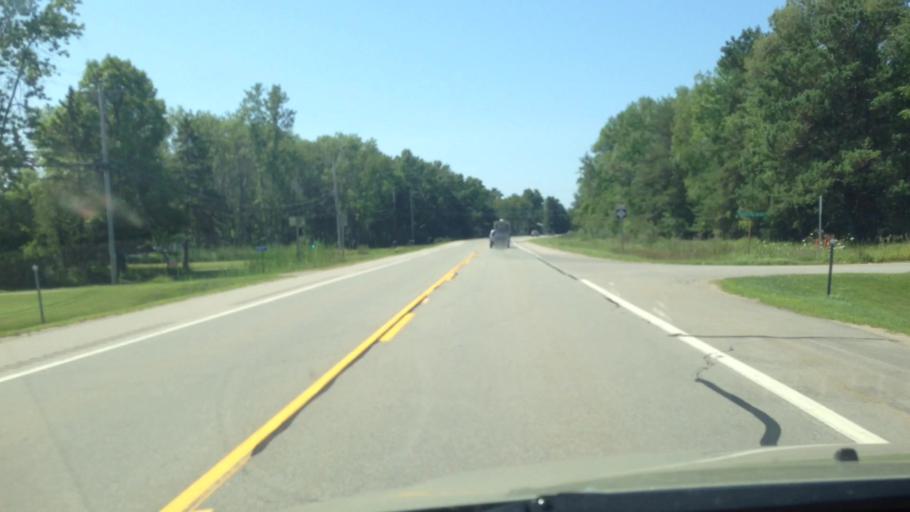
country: US
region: Michigan
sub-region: Menominee County
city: Menominee
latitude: 45.1780
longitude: -87.5699
